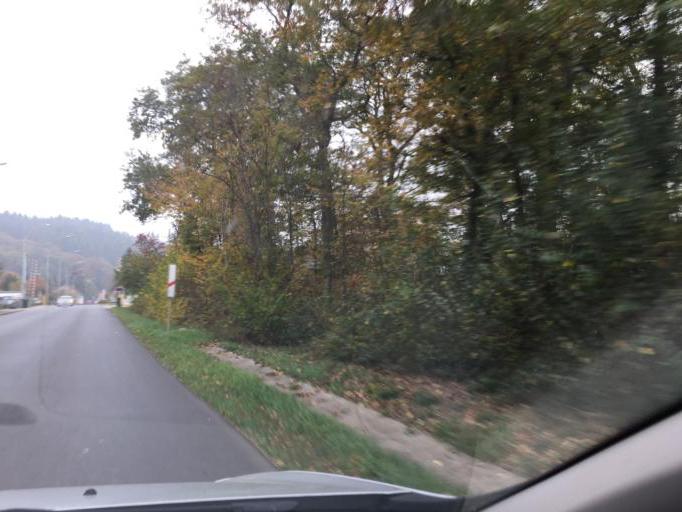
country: LU
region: Luxembourg
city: Moutfort
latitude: 49.5921
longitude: 6.2532
